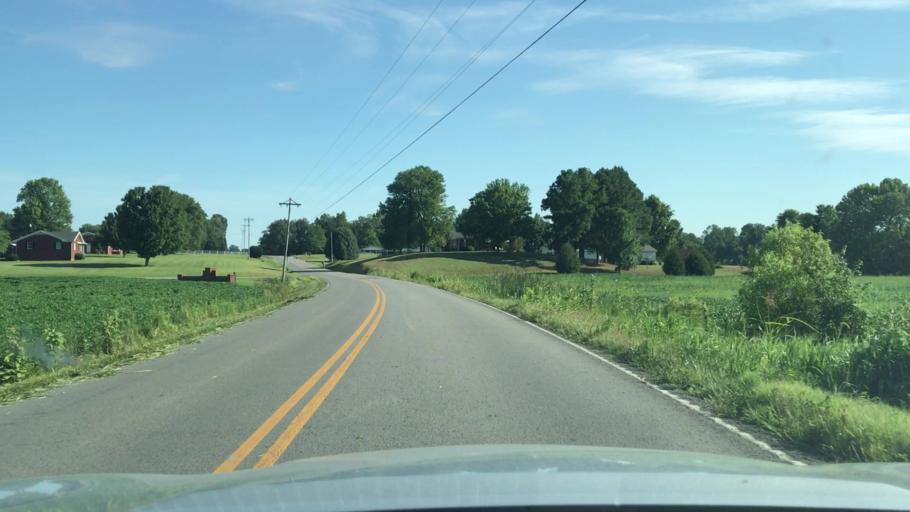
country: US
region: Kentucky
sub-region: Muhlenberg County
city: Greenville
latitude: 37.1450
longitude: -87.1412
